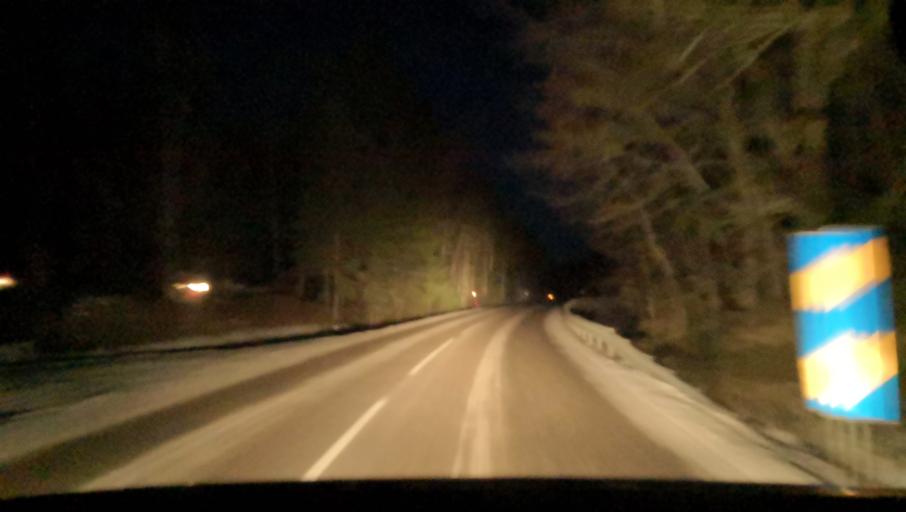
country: SE
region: Soedermanland
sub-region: Flens Kommun
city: Halleforsnas
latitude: 59.1976
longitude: 16.4793
